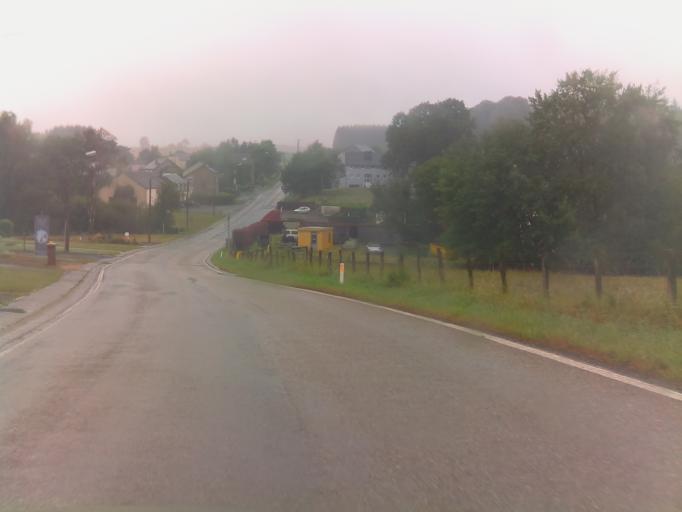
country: BE
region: Wallonia
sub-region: Province du Luxembourg
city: Paliseul
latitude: 49.9032
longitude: 5.1283
